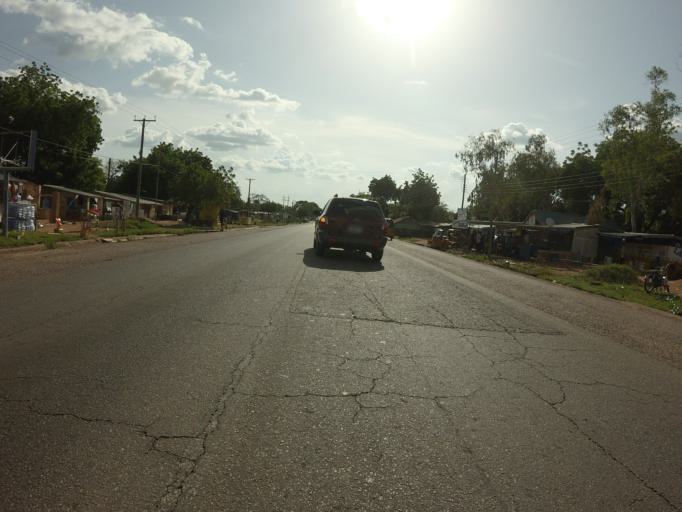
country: GH
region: Upper East
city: Bolgatanga
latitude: 10.8025
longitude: -0.8655
